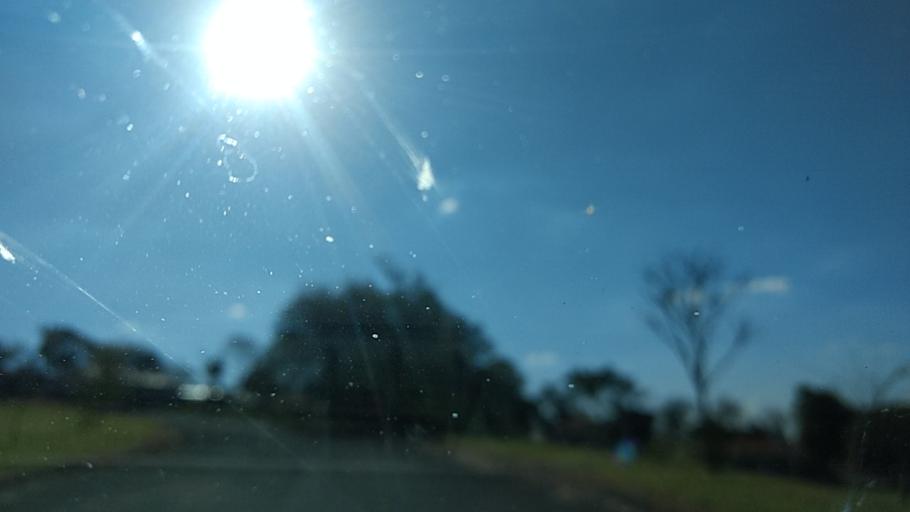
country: BR
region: Sao Paulo
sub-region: Botucatu
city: Botucatu
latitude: -22.8462
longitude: -48.4331
